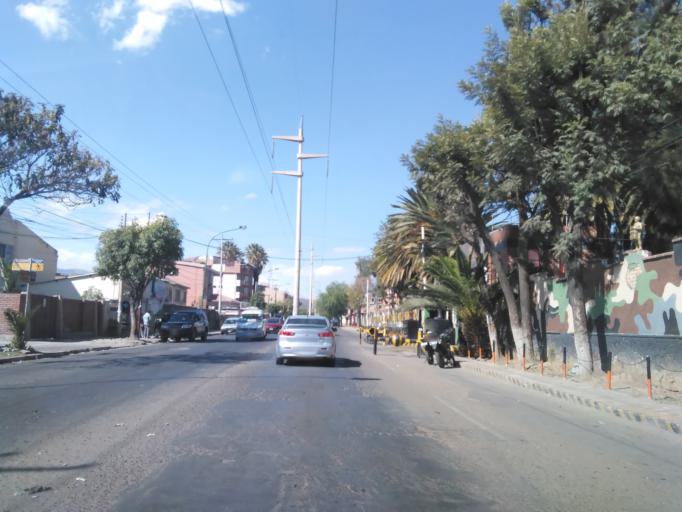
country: BO
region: Cochabamba
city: Cochabamba
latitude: -17.3965
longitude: -66.1725
